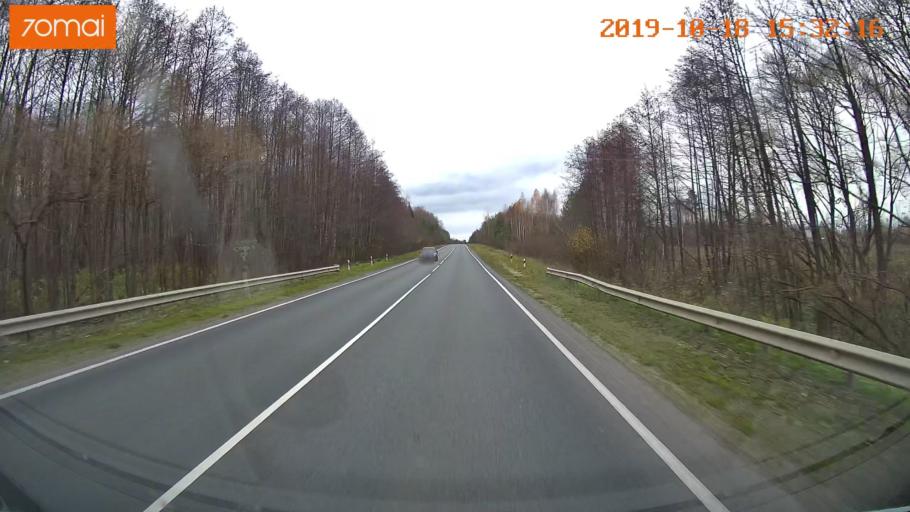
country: RU
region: Vladimir
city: Anopino
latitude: 55.8236
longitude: 40.6553
